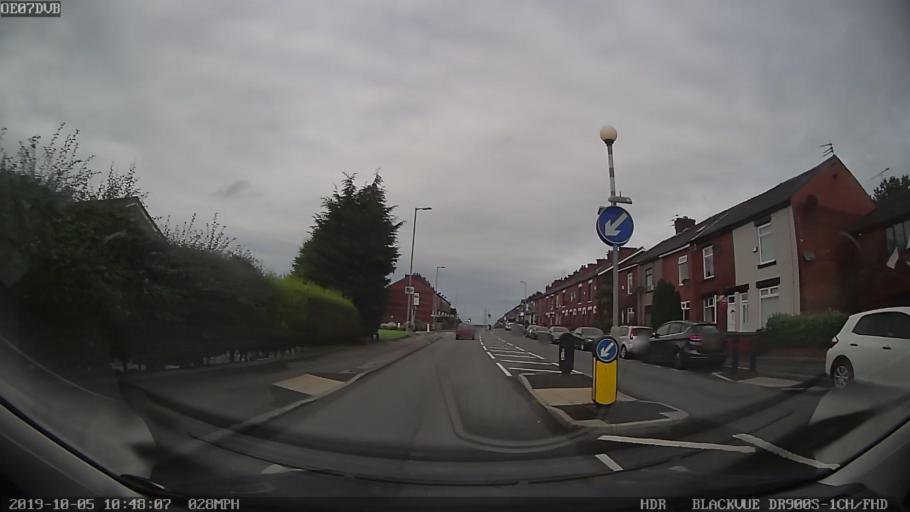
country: GB
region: England
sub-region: Borough of Rochdale
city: Middleton
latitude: 53.5491
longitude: -2.1609
